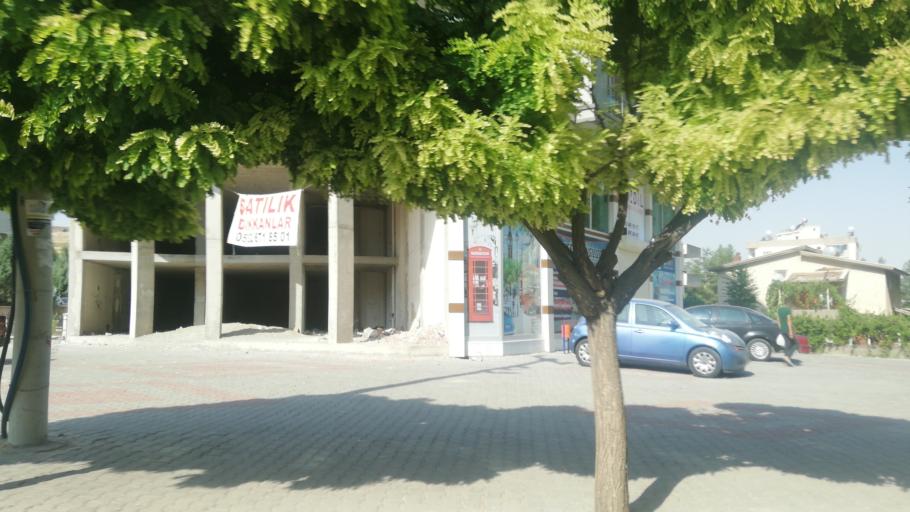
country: TR
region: Mardin
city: Midyat
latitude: 37.4319
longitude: 41.3365
